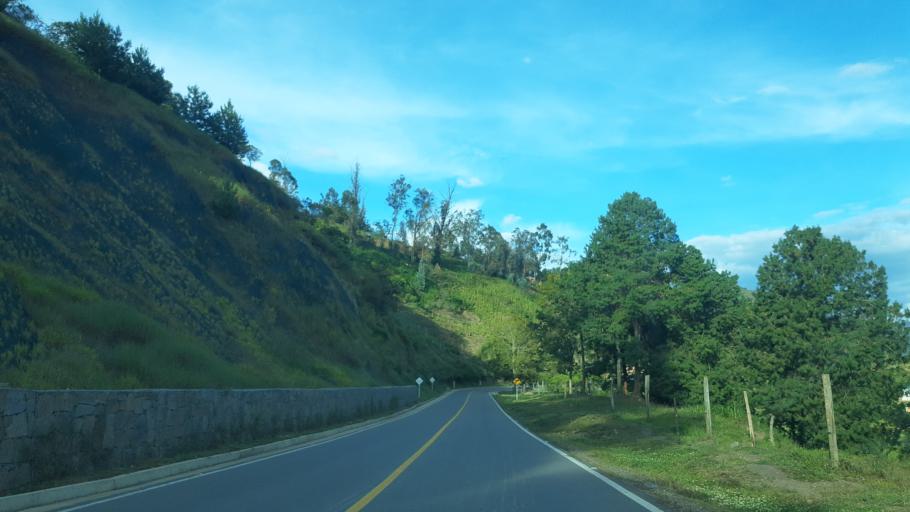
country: CO
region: Cundinamarca
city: Macheta
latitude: 5.0727
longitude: -73.5971
